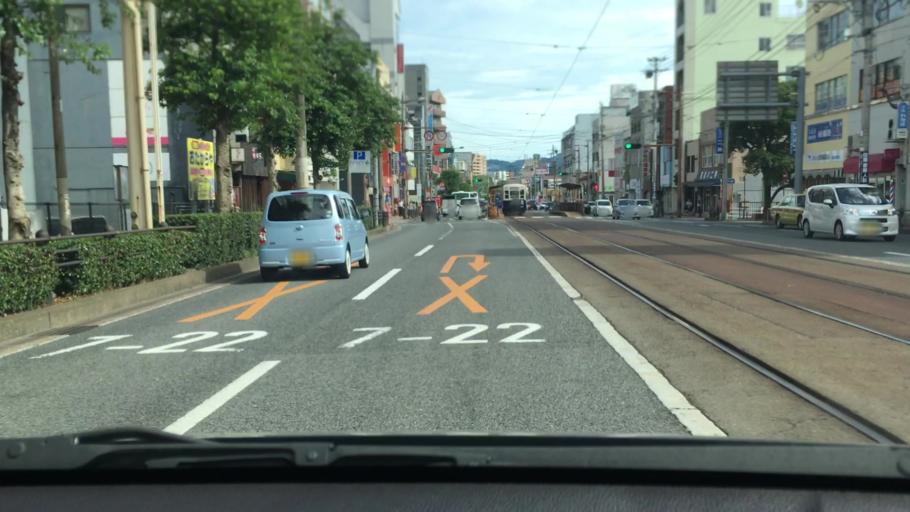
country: JP
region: Nagasaki
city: Obita
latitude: 32.7904
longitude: 129.8608
